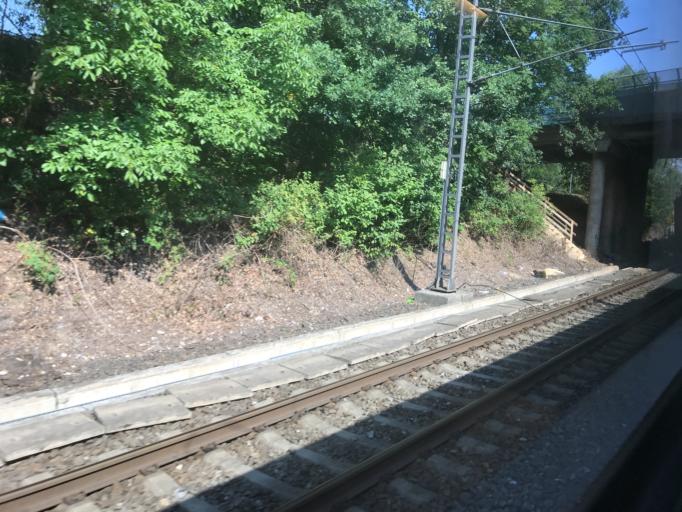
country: CZ
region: Central Bohemia
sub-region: Okres Praha-Vychod
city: Ricany
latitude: 49.9920
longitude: 14.6698
